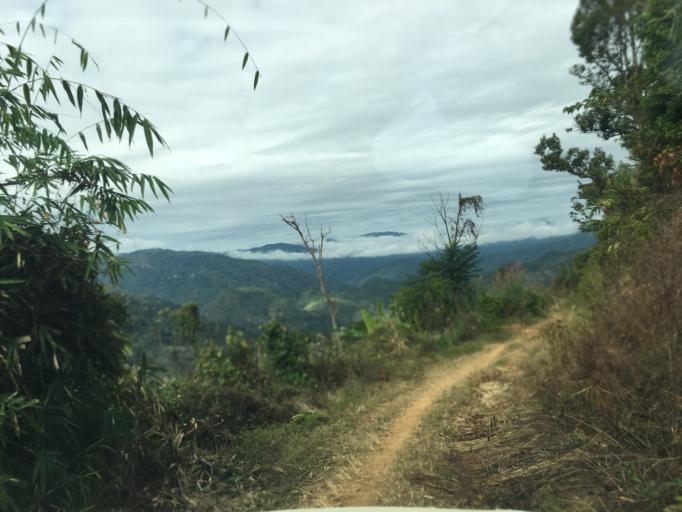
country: LA
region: Houaphan
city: Viengthong
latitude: 19.9206
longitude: 103.2969
